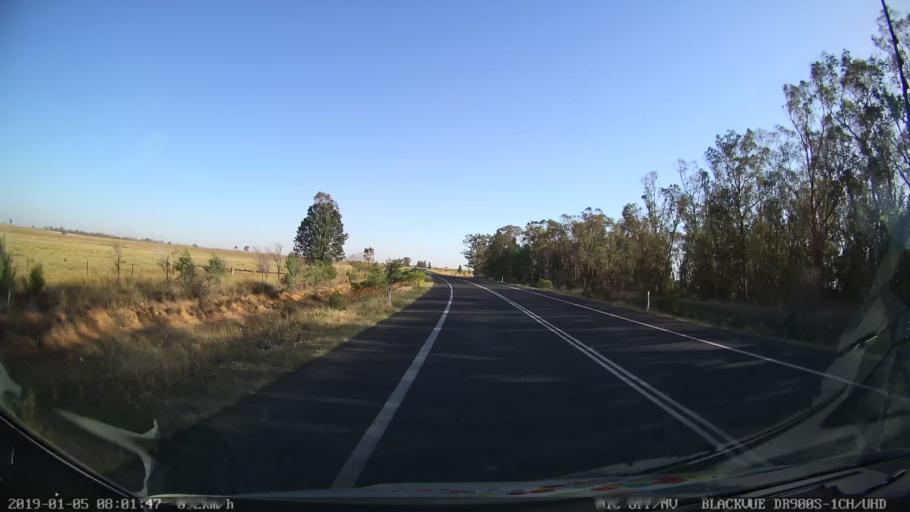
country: AU
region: New South Wales
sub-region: Gilgandra
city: Gilgandra
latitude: -31.6835
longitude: 148.7065
